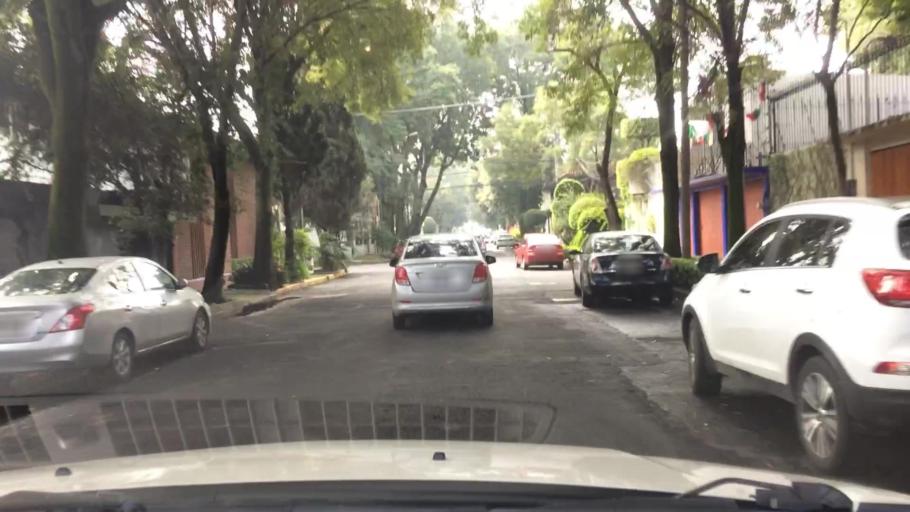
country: MX
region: Mexico City
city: Coyoacan
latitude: 19.3554
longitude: -99.1576
